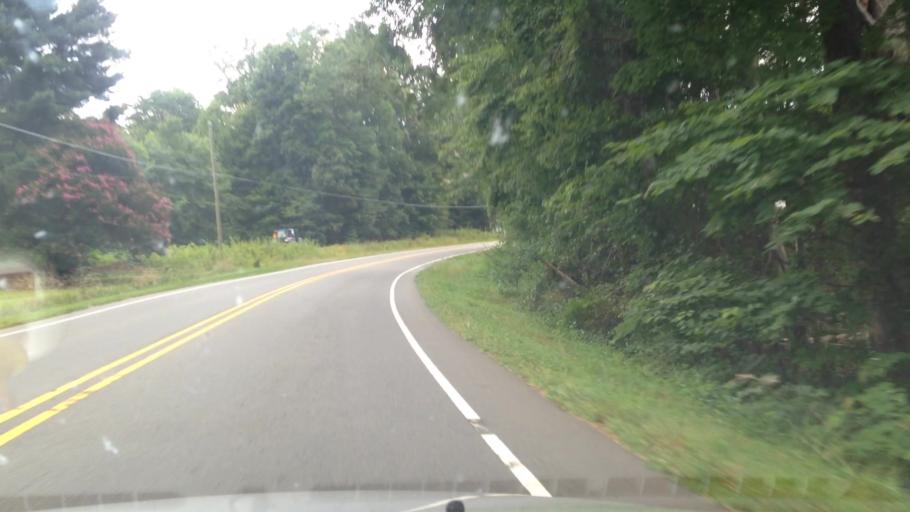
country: US
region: North Carolina
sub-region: Rockingham County
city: Wentworth
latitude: 36.4015
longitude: -79.7788
